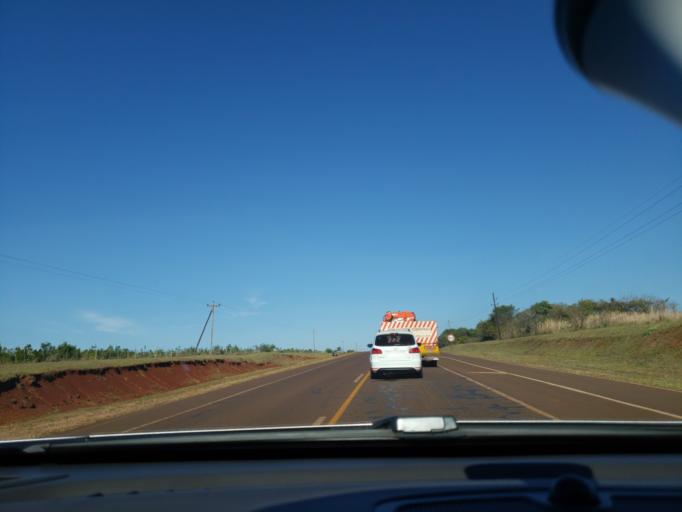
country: AR
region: Misiones
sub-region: Departamento de Apostoles
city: San Jose
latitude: -27.7558
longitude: -55.7755
